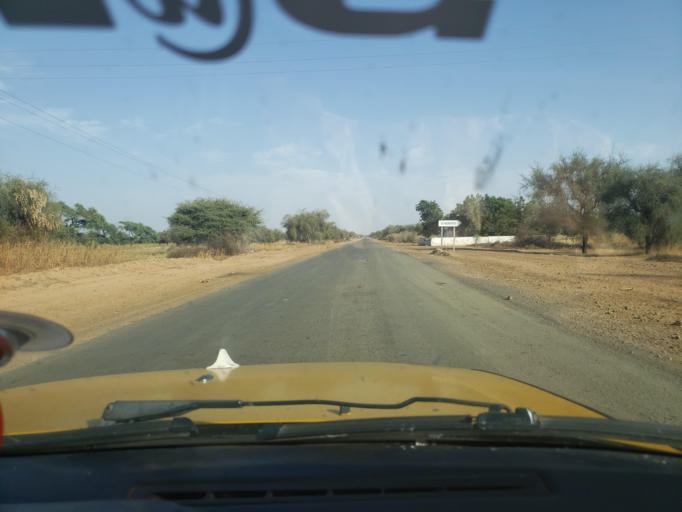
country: SN
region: Louga
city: Louga
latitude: 15.5030
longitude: -15.9479
